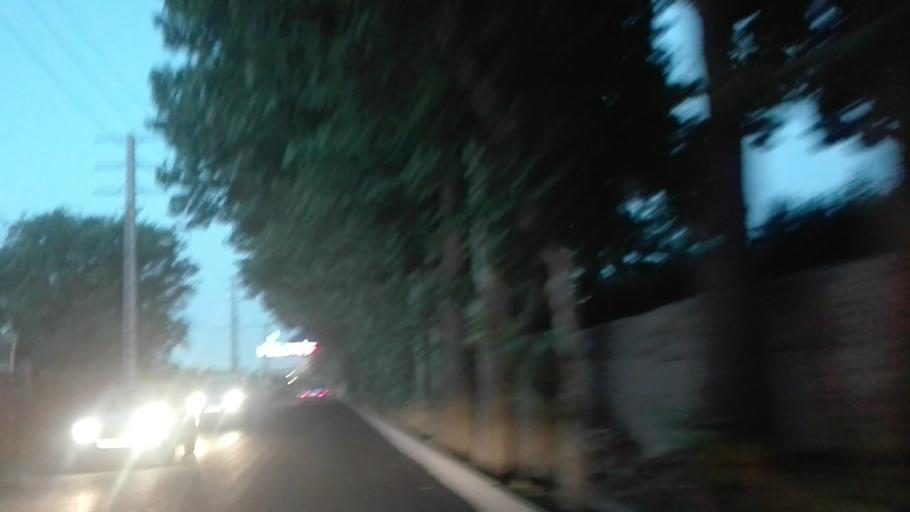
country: IR
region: Tehran
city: Shahriar
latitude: 35.6409
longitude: 51.0573
